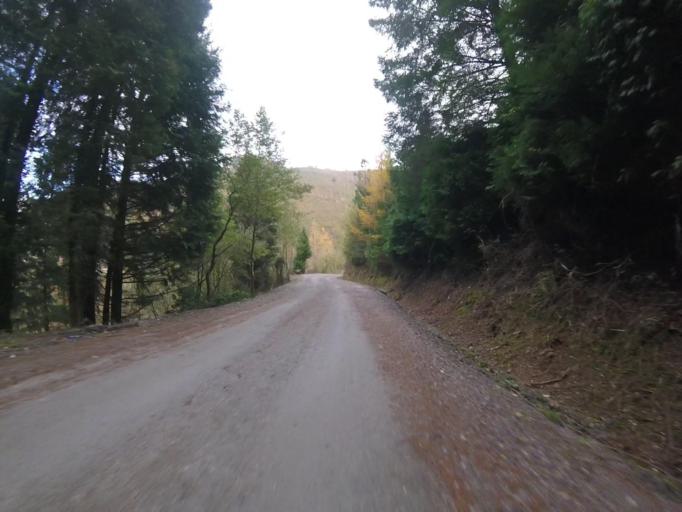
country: ES
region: Navarre
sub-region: Provincia de Navarra
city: Goizueta
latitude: 43.2089
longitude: -1.8536
